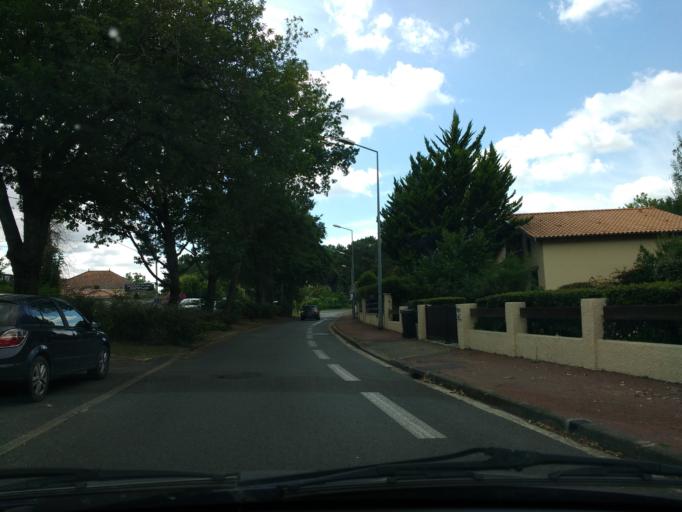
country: FR
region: Aquitaine
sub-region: Departement de la Gironde
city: Gradignan
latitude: 44.7708
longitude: -0.6079
